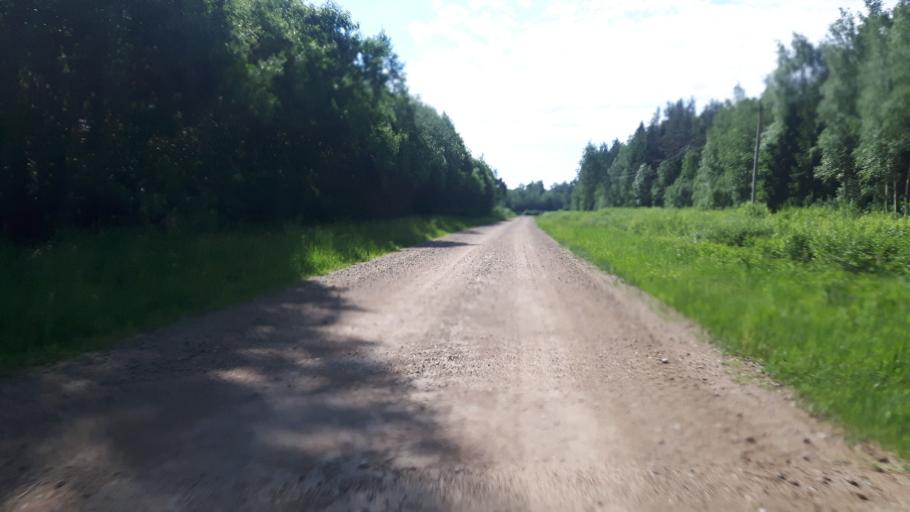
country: EE
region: Paernumaa
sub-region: Vaendra vald (alev)
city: Vandra
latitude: 58.6952
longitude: 25.0317
